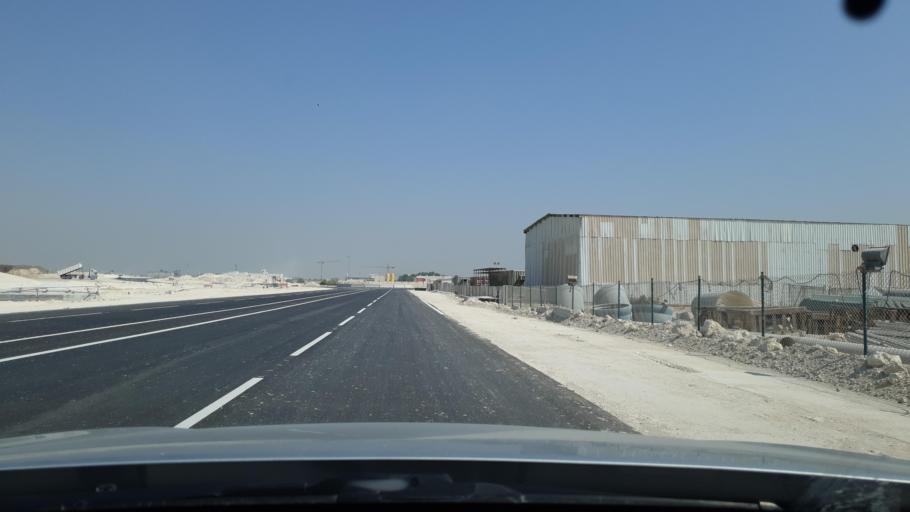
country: QA
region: Baladiyat ad Dawhah
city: Doha
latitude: 25.2233
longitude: 51.5199
